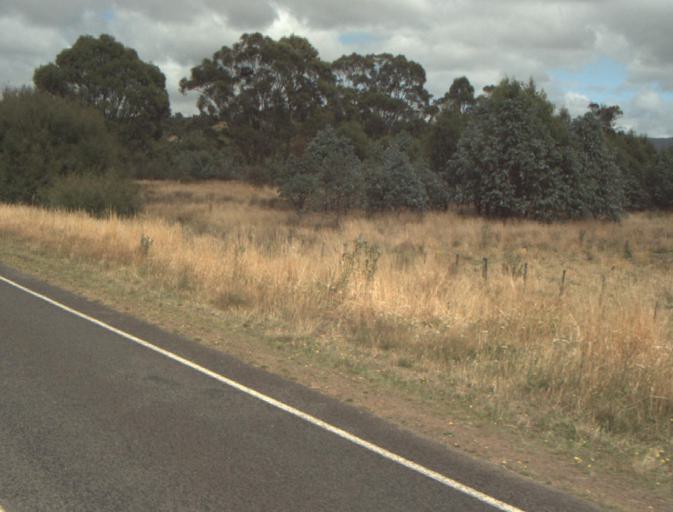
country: AU
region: Tasmania
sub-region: Northern Midlands
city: Evandale
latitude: -41.4771
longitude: 147.5368
